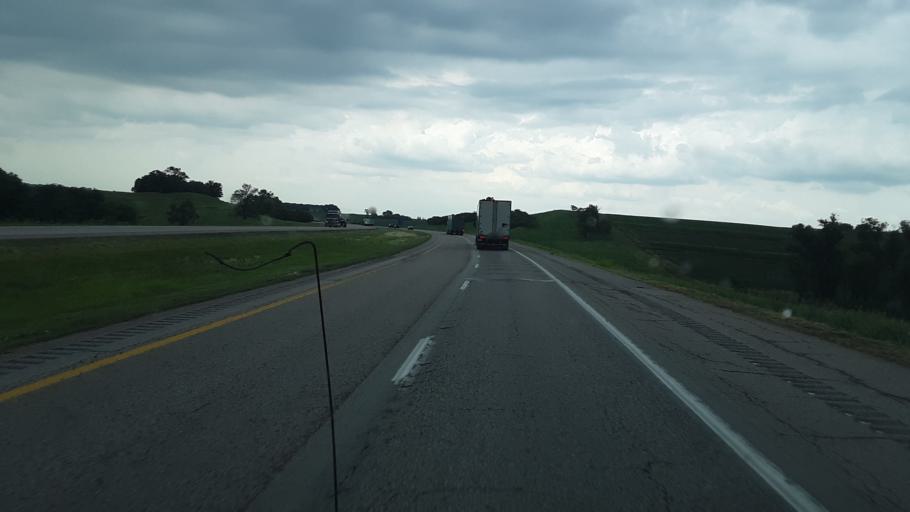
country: US
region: Iowa
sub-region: Pottawattamie County
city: Council Bluffs
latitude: 41.3808
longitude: -95.6708
